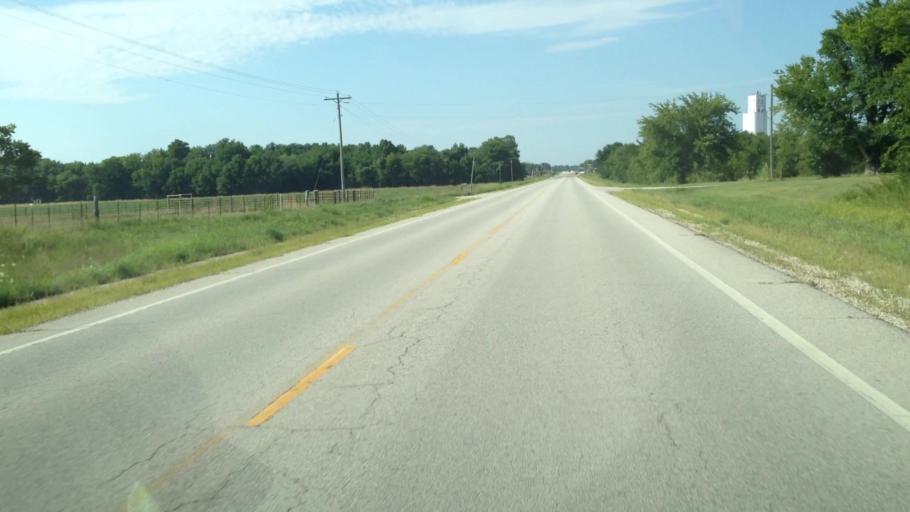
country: US
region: Kansas
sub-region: Neosho County
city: Erie
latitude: 37.5097
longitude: -95.2699
